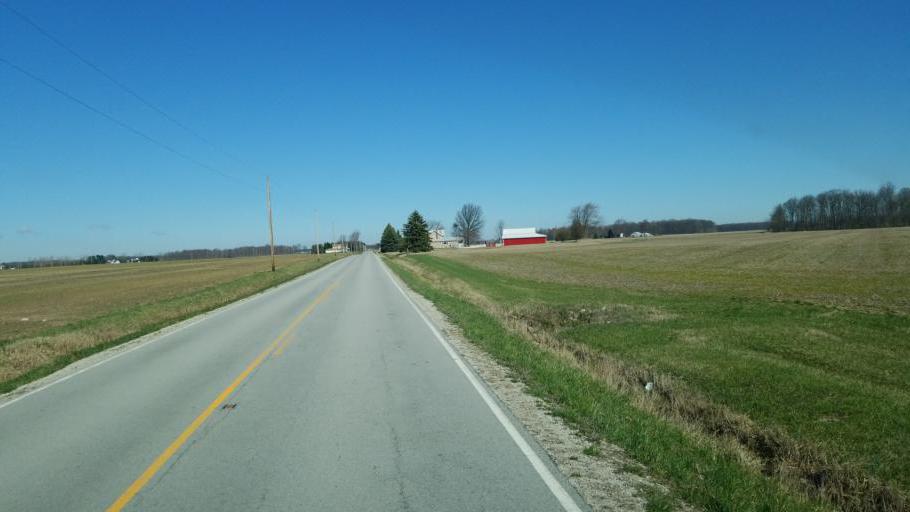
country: US
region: Ohio
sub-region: Huron County
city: Willard
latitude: 41.0303
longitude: -82.8726
